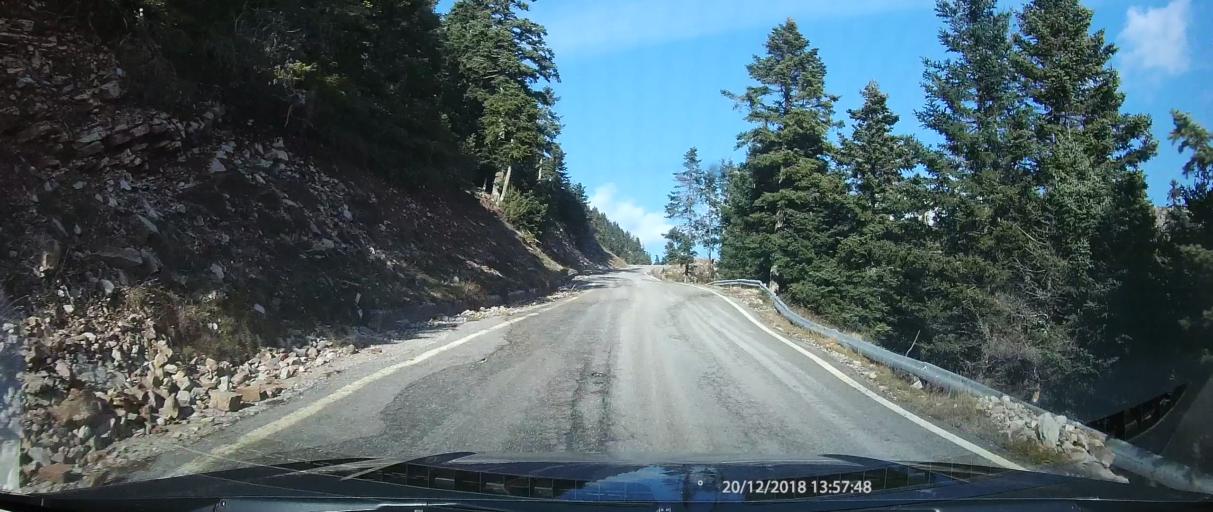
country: GR
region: West Greece
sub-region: Nomos Aitolias kai Akarnanias
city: Thermo
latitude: 38.7123
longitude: 21.6217
